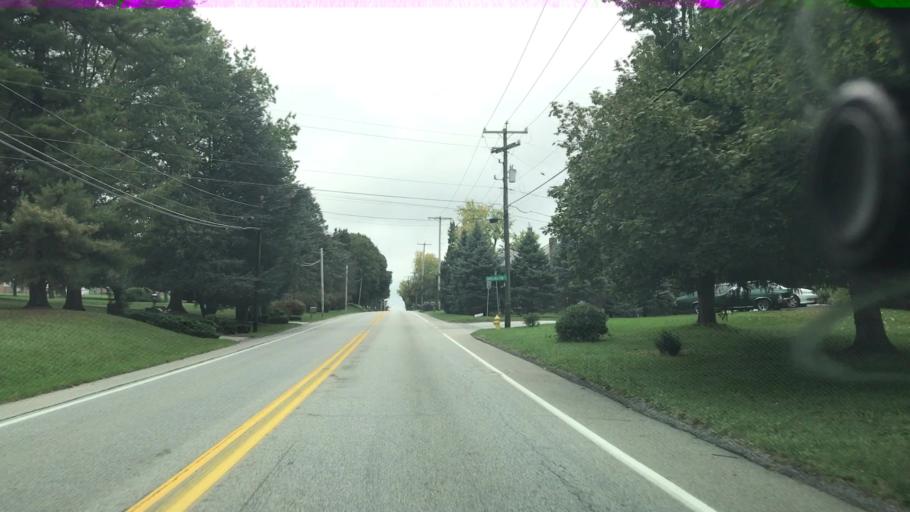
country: US
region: Pennsylvania
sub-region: York County
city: Weigelstown
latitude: 39.9234
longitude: -76.8270
